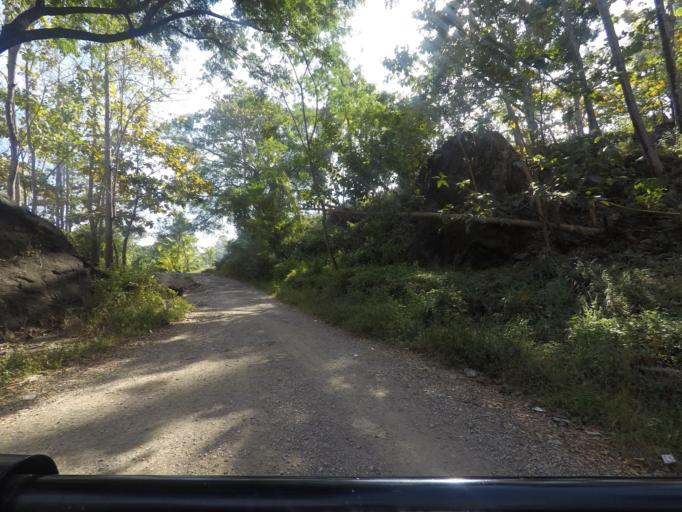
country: TL
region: Bobonaro
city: Maliana
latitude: -8.9981
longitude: 125.2234
